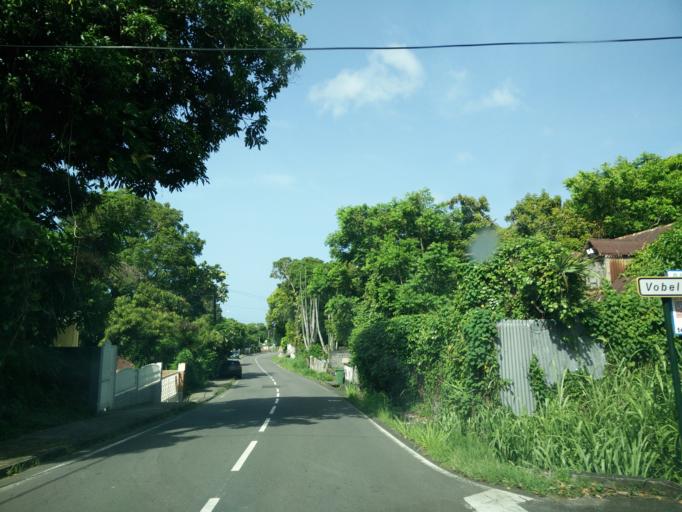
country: GP
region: Guadeloupe
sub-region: Guadeloupe
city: Gourbeyre
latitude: 15.9917
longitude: -61.7073
